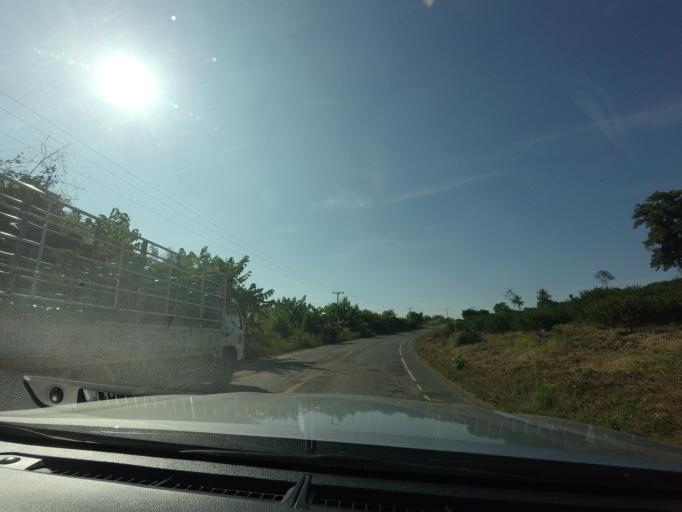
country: TH
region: Phrae
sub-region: Amphoe Wang Chin
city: Wang Chin
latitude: 17.7055
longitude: 99.6839
